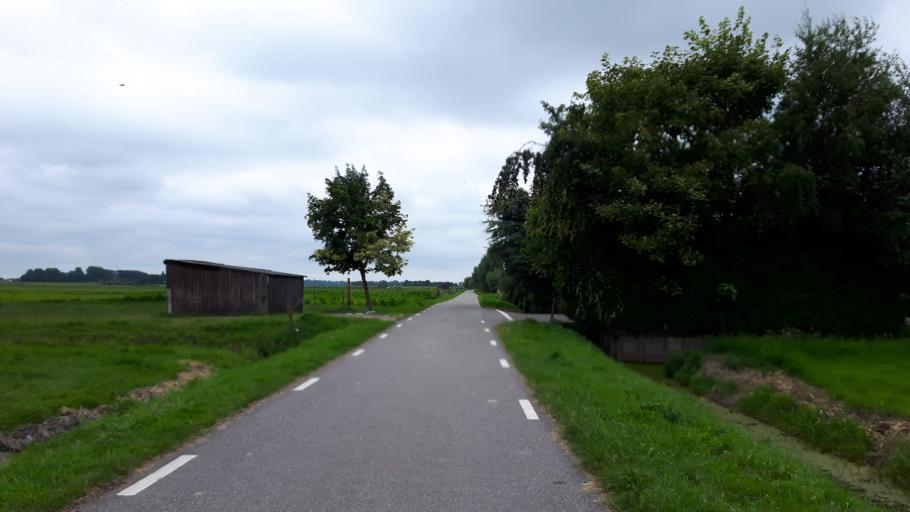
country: NL
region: South Holland
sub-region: Gemeente Pijnacker-Nootdorp
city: Pijnacker
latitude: 51.9896
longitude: 4.4347
